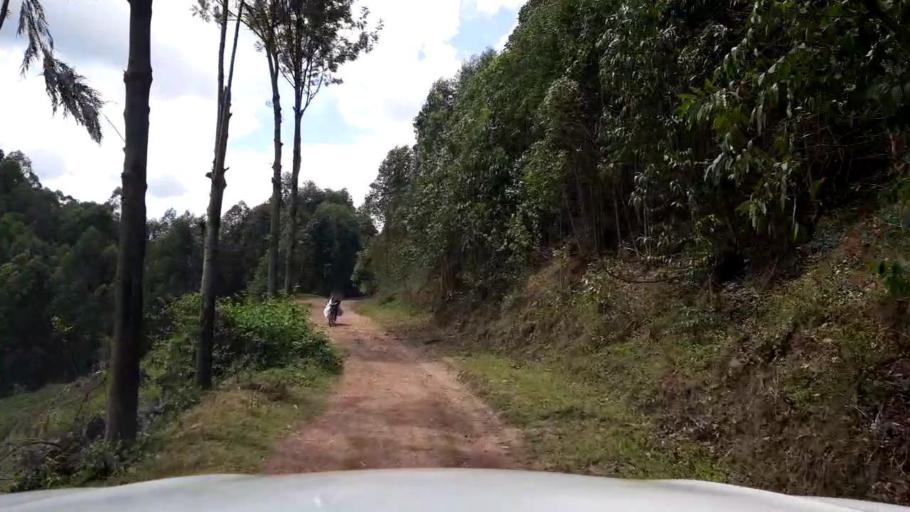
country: RW
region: Northern Province
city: Byumba
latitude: -1.5217
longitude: 30.1296
